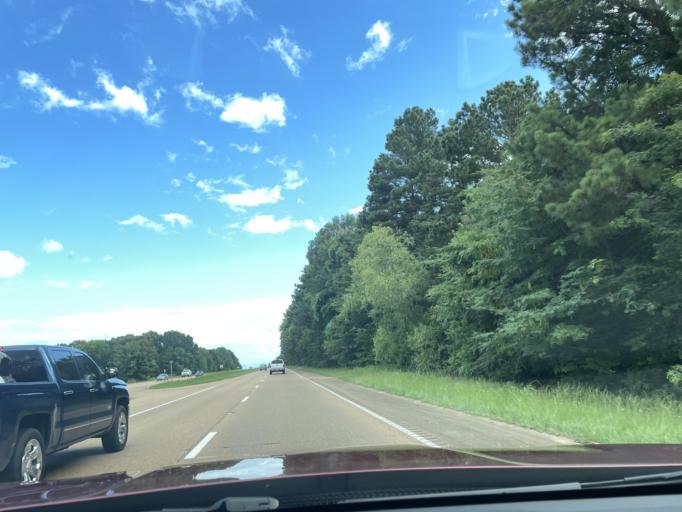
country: US
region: Mississippi
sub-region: Madison County
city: Flora
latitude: 32.5209
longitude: -90.3072
